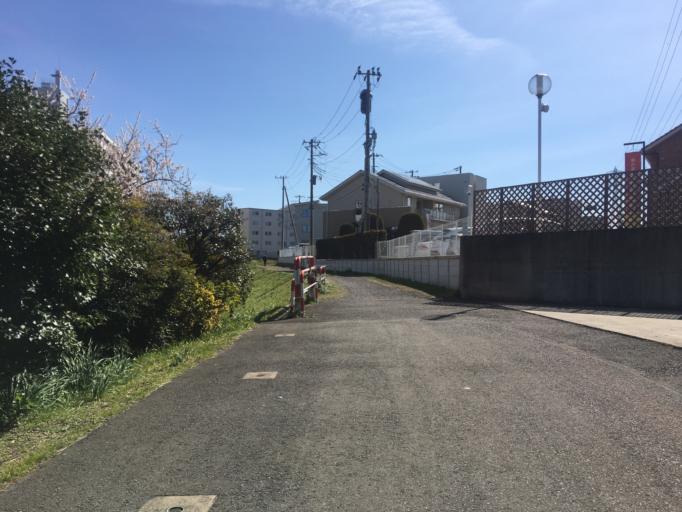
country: JP
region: Saitama
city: Asaka
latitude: 35.7941
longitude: 139.5789
